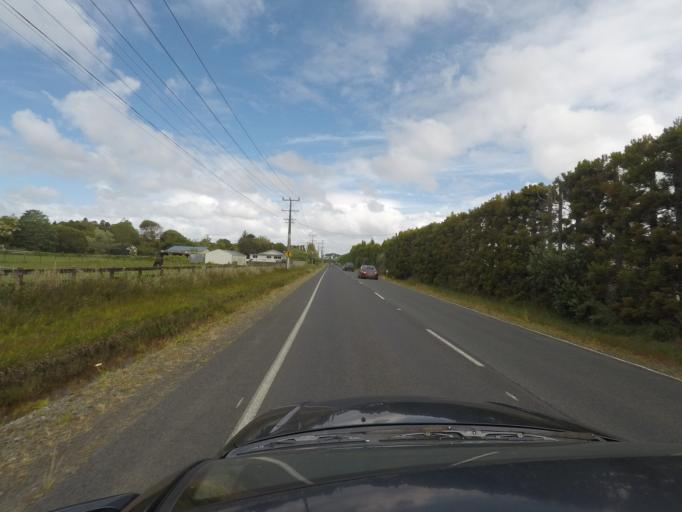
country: NZ
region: Auckland
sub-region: Auckland
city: Muriwai Beach
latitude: -36.7752
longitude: 174.5754
